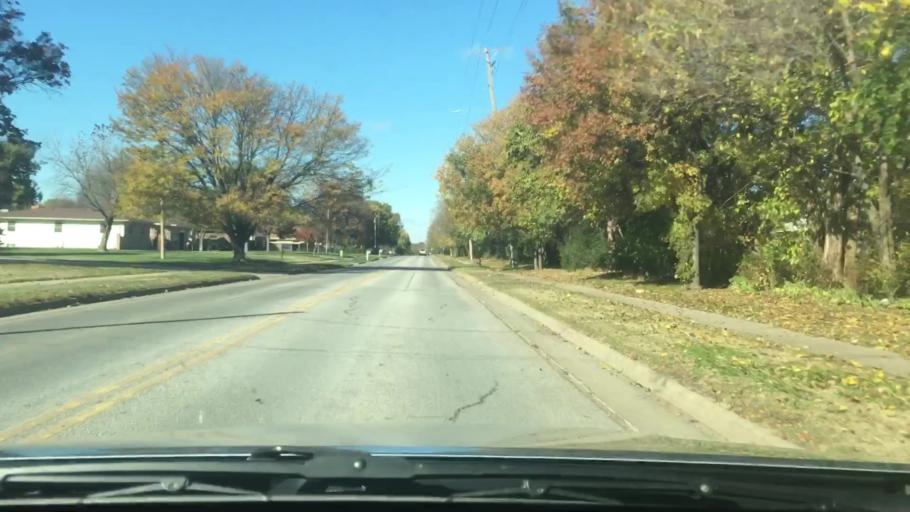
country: US
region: Kansas
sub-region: Sedgwick County
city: Maize
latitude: 37.6960
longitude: -97.4807
